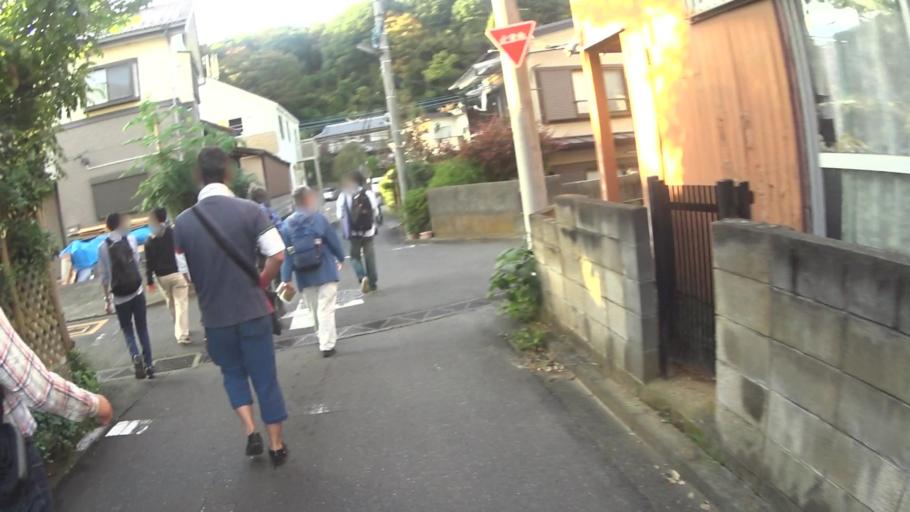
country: JP
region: Tokyo
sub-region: Machida-shi
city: Machida
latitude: 35.5826
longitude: 139.4472
